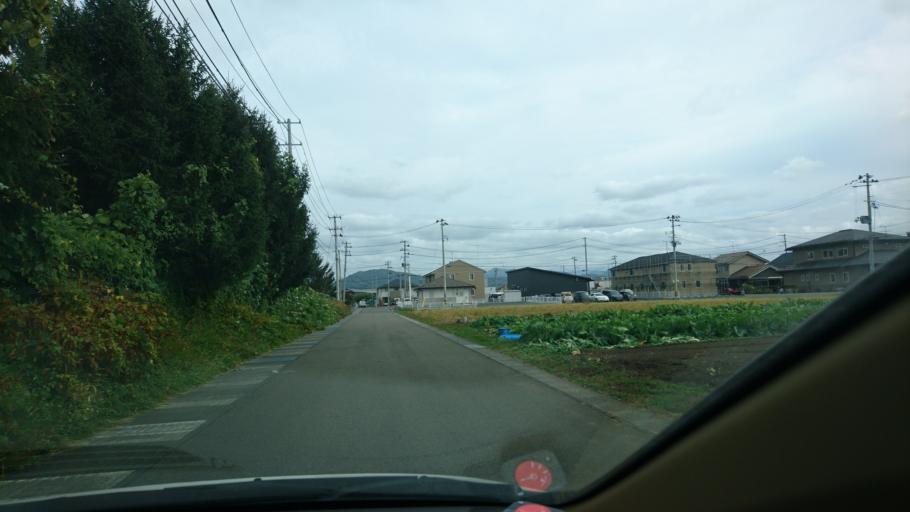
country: JP
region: Iwate
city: Morioka-shi
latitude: 39.6746
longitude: 141.1306
